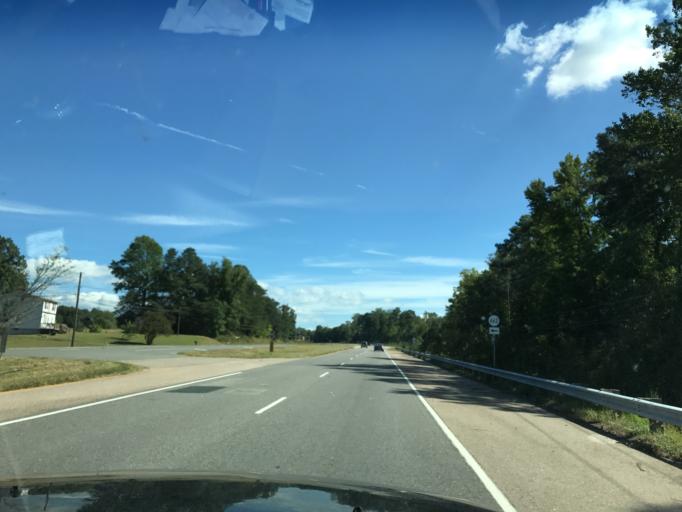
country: US
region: Virginia
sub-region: Essex County
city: Tappahannock
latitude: 37.8655
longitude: -76.8390
